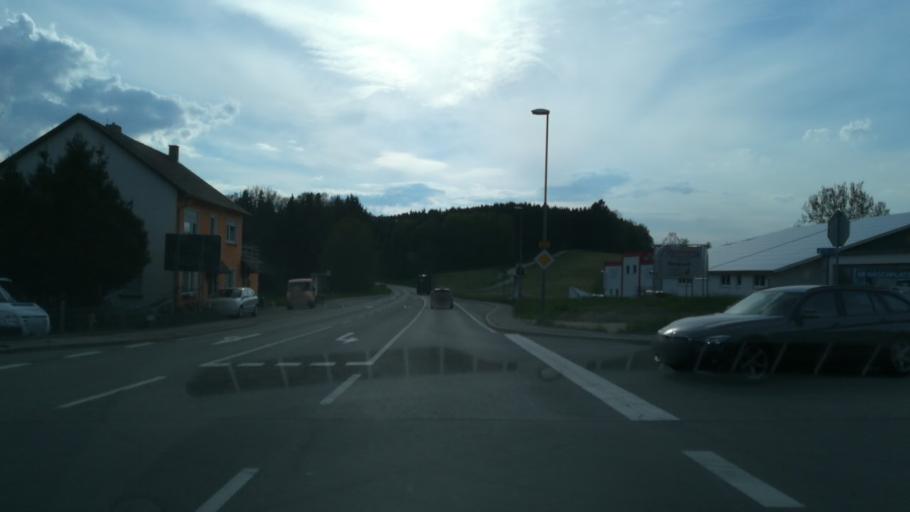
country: DE
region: Baden-Wuerttemberg
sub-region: Freiburg Region
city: Muhlingen
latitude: 47.9056
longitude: 9.0289
